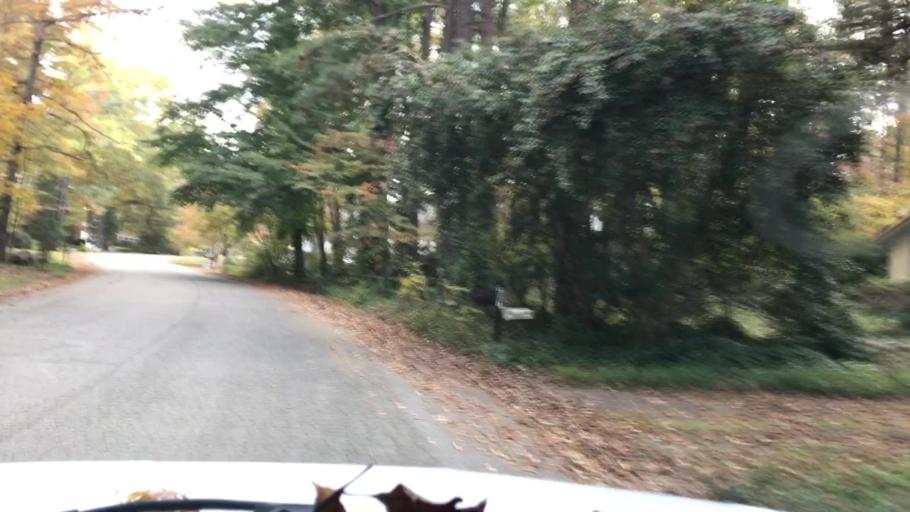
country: US
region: Virginia
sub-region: Henrico County
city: Short Pump
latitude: 37.6057
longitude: -77.7132
